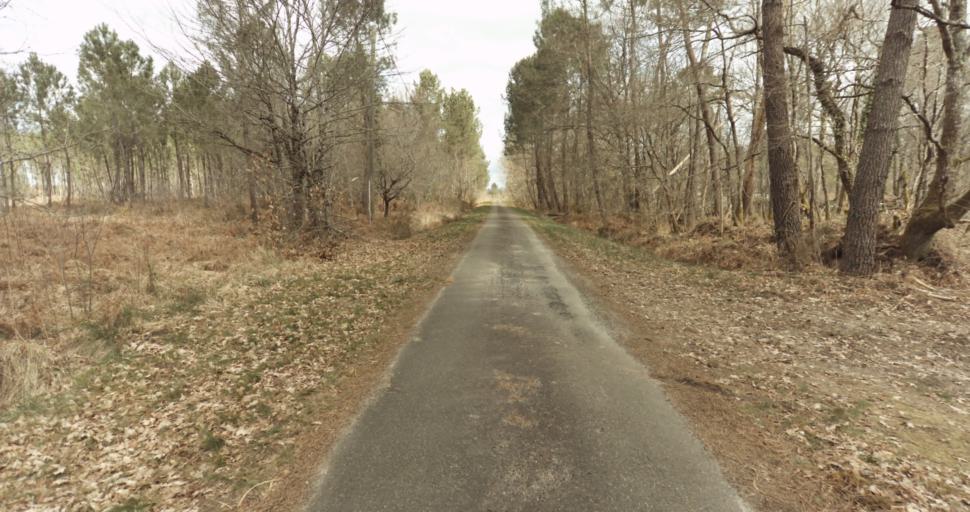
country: FR
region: Aquitaine
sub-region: Departement des Landes
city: Roquefort
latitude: 44.0808
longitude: -0.3933
